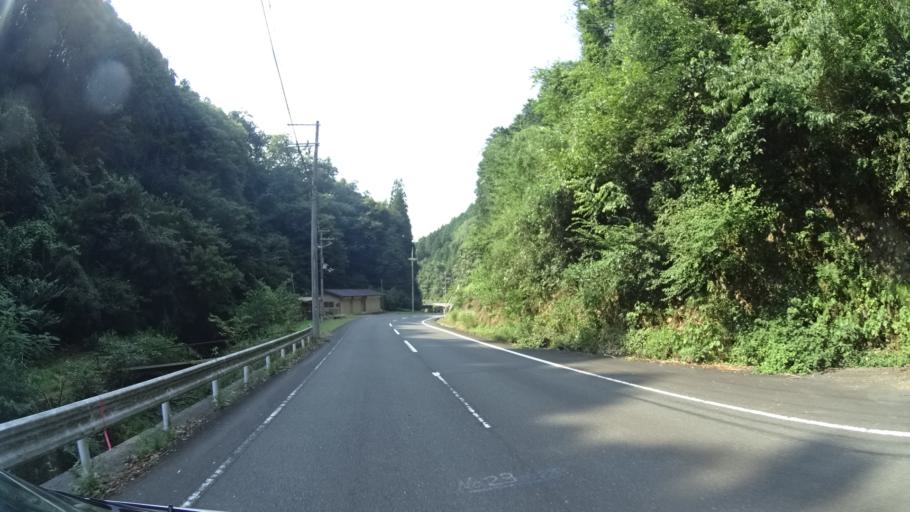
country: JP
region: Kyoto
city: Maizuru
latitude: 35.4138
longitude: 135.2311
